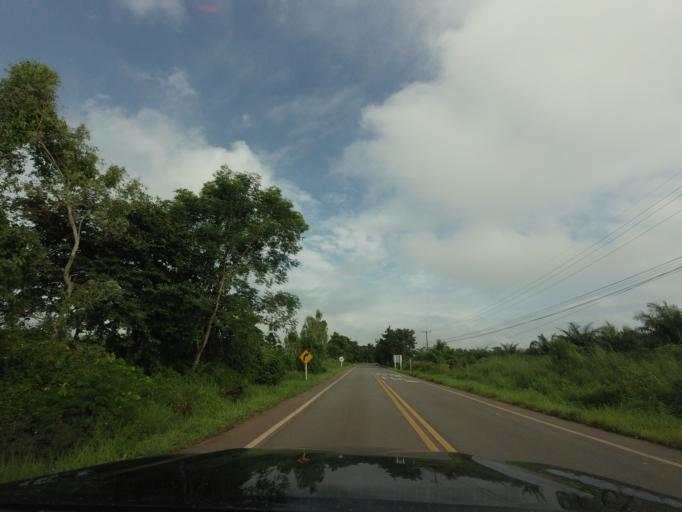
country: TH
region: Changwat Udon Thani
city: Nam Som
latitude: 17.8078
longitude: 102.2719
